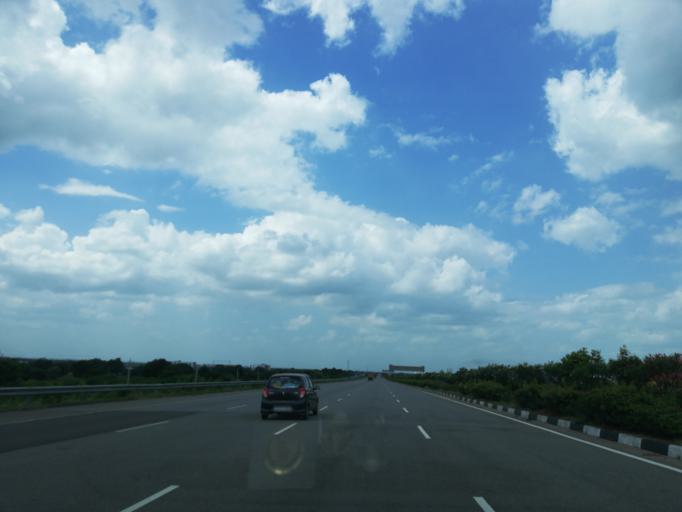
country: IN
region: Telangana
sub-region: Medak
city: Serilingampalle
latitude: 17.4739
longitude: 78.2478
